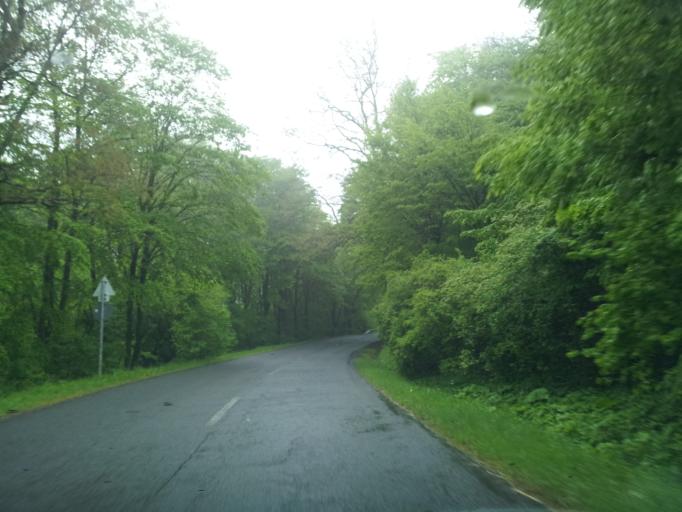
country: HU
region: Baranya
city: Hosszuheteny
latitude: 46.1899
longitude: 18.3205
